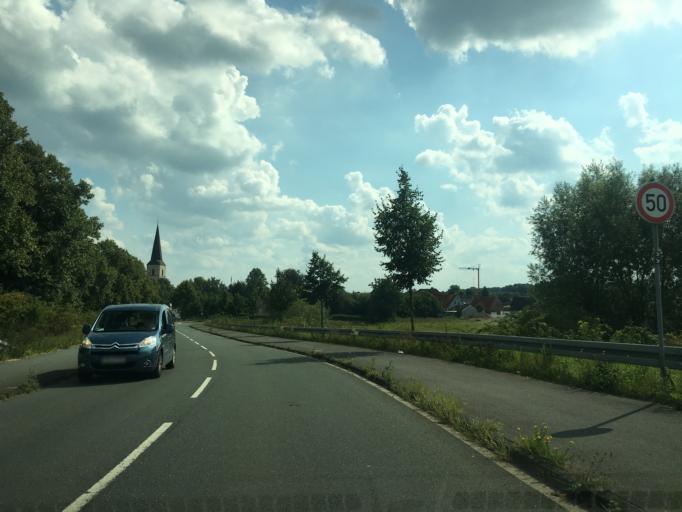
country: DE
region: North Rhine-Westphalia
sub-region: Regierungsbezirk Munster
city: Muenster
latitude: 51.8874
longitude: 7.6012
